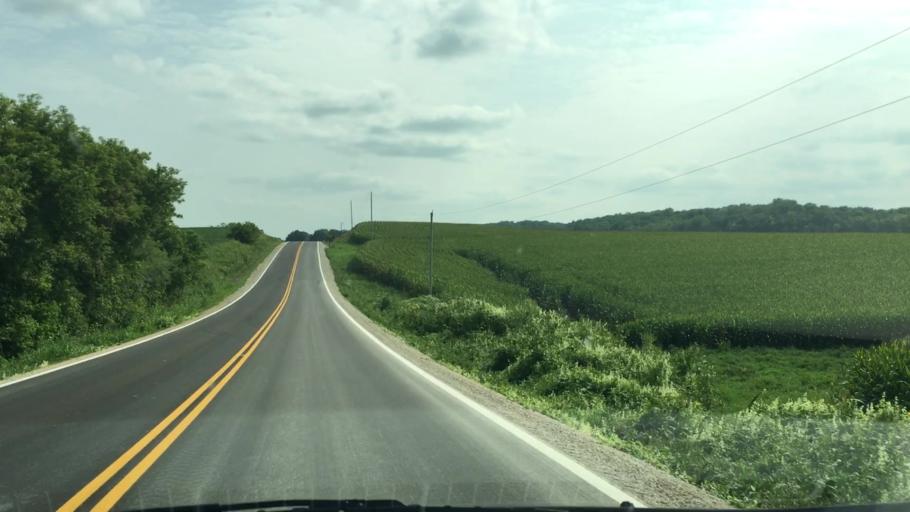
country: US
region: Minnesota
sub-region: Fillmore County
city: Preston
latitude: 43.7499
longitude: -92.0200
